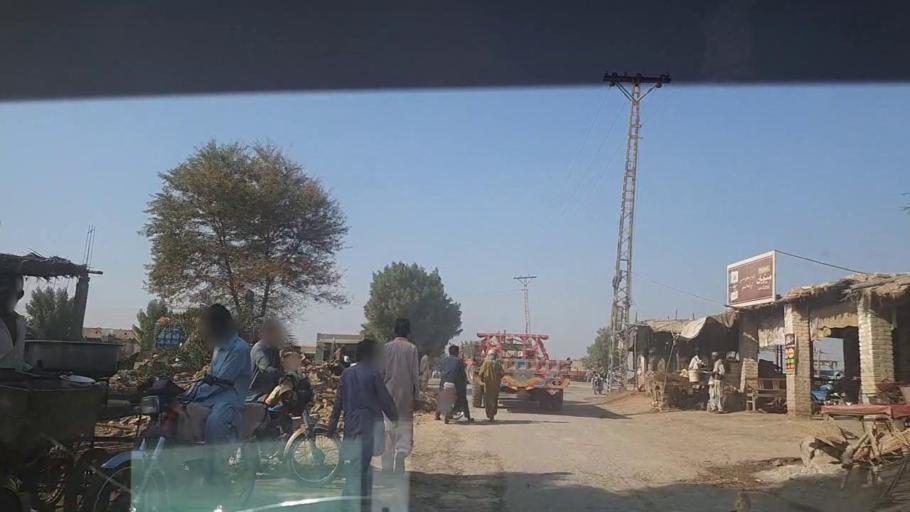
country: PK
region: Sindh
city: Kot Diji
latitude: 27.4399
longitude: 68.6325
